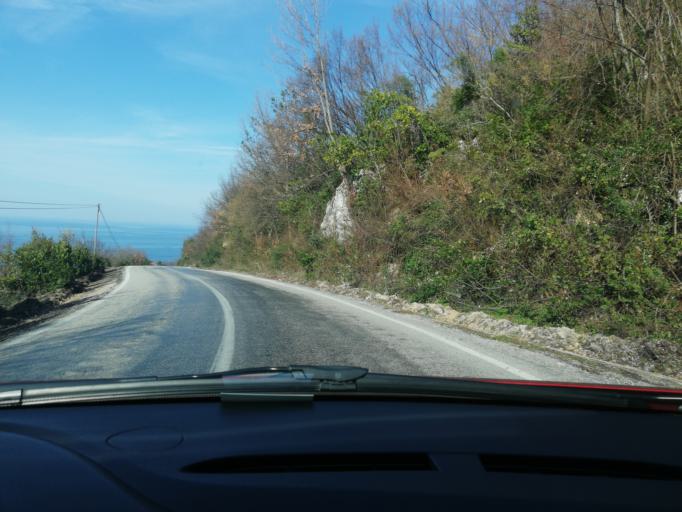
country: TR
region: Bartin
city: Kurucasile
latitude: 41.8480
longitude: 32.7705
